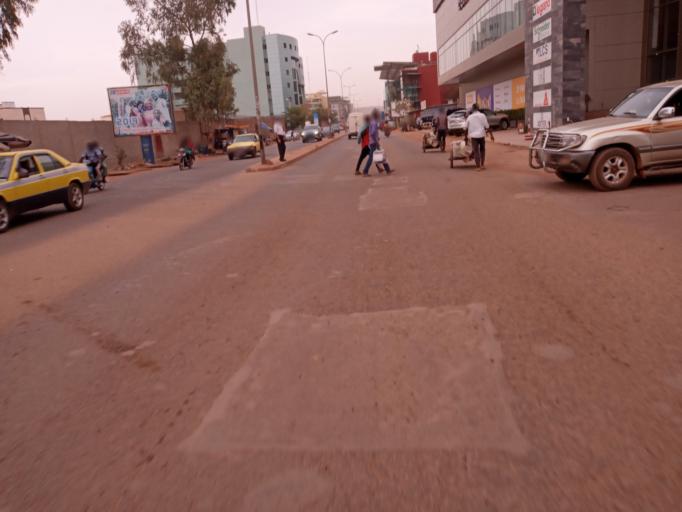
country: ML
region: Bamako
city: Bamako
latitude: 12.6316
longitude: -8.0288
